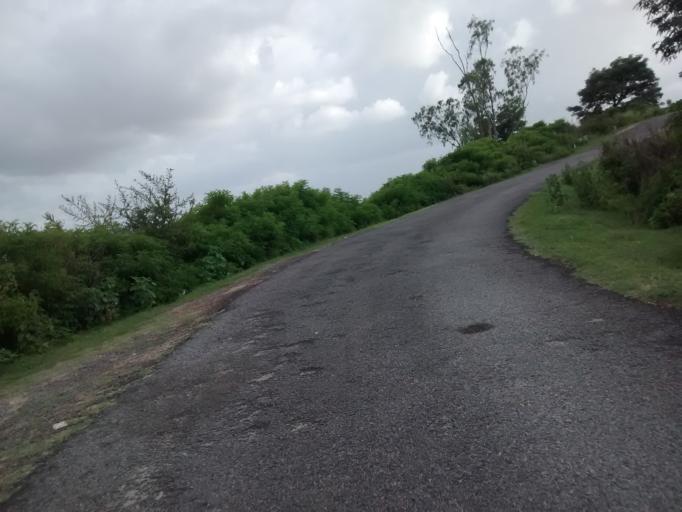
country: IN
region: Karnataka
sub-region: Tumkur
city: Tumkur
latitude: 13.3744
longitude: 77.2141
